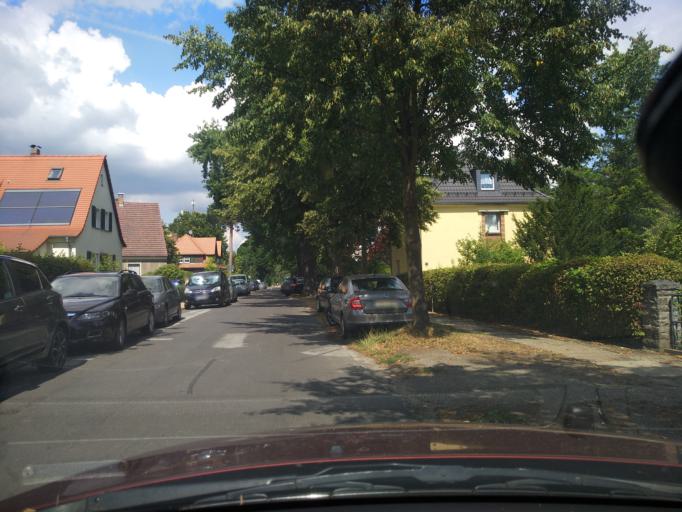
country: DE
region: Saxony
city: Niesky
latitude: 51.2960
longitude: 14.8189
